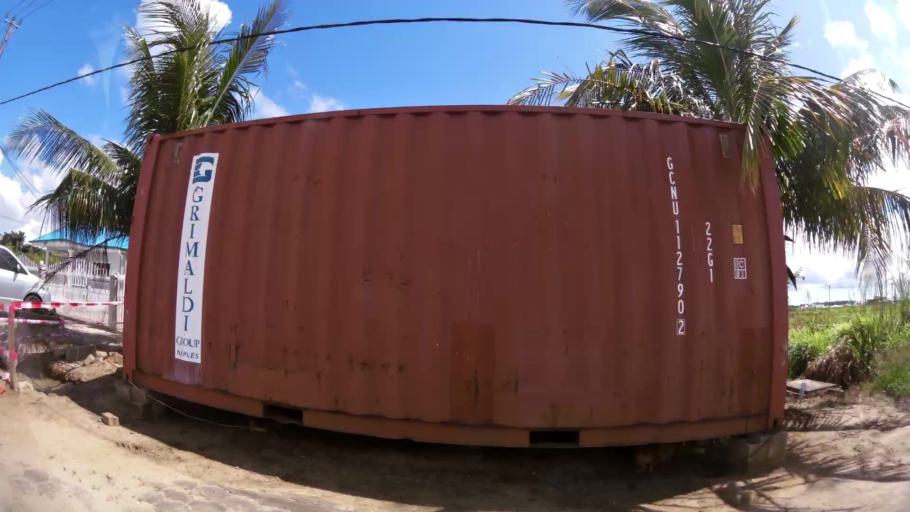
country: SR
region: Paramaribo
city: Paramaribo
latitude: 5.8716
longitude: -55.1332
